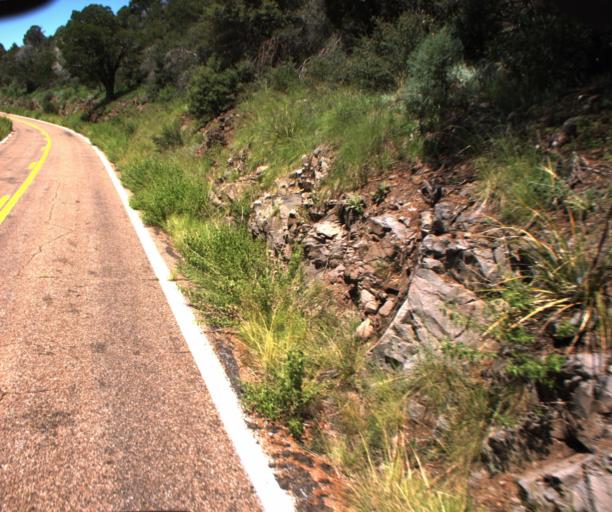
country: US
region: Arizona
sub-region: Greenlee County
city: Morenci
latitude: 33.4855
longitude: -109.3523
